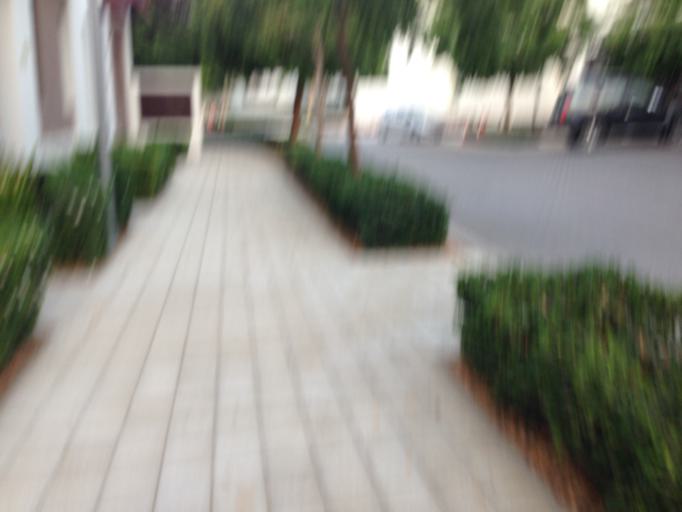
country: OM
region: Muhafazat Masqat
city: As Sib al Jadidah
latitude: 23.6288
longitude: 58.2690
